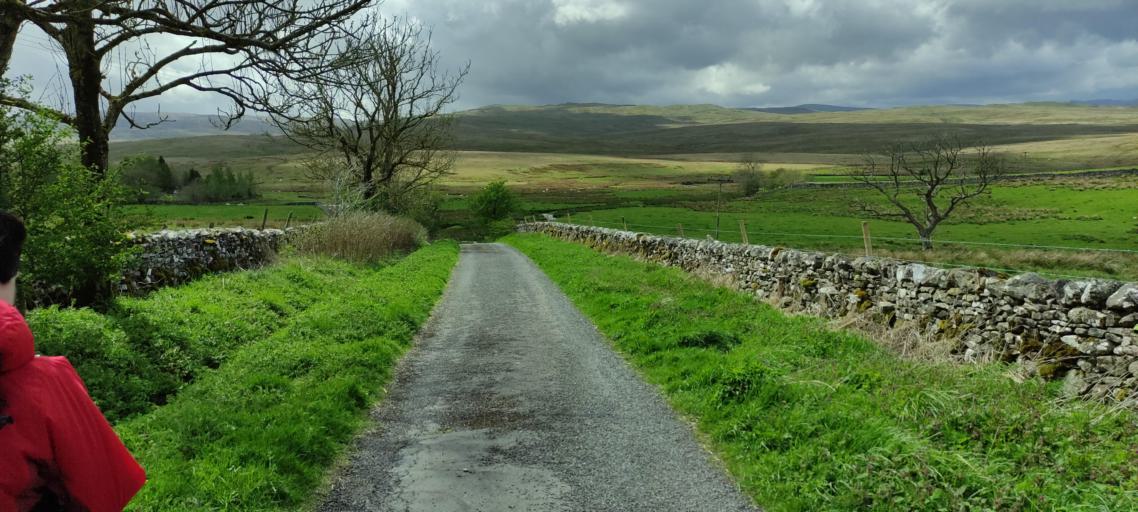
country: GB
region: England
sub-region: Cumbria
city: Penrith
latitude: 54.5187
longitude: -2.6789
